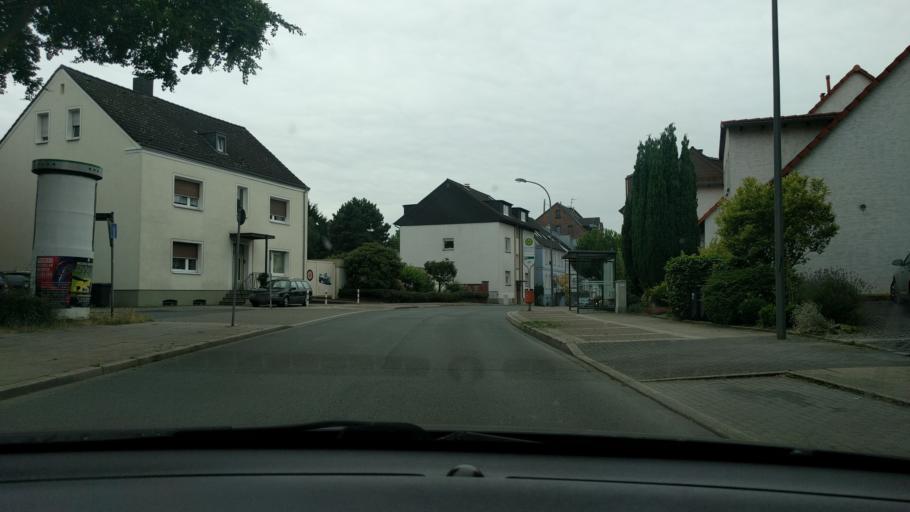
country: DE
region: North Rhine-Westphalia
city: Witten
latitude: 51.4773
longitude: 7.3377
